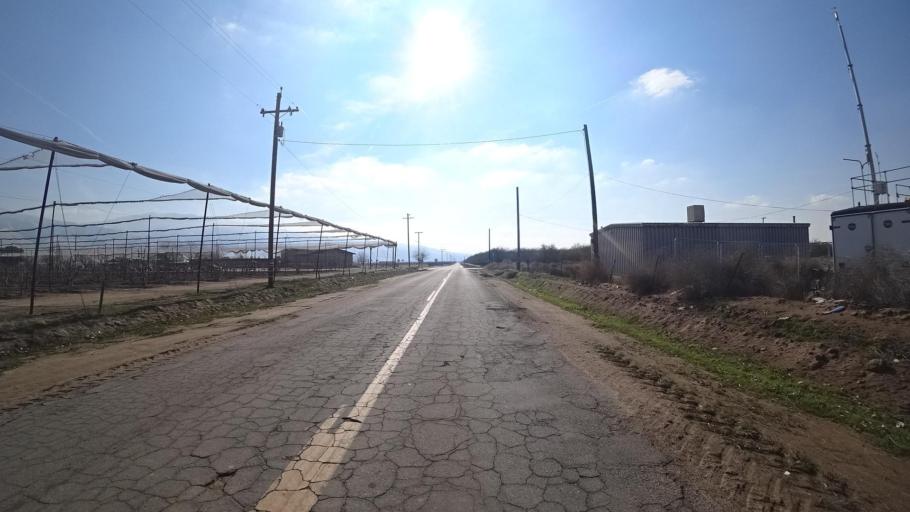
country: US
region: California
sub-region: Kern County
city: Arvin
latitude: 35.2393
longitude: -118.7885
